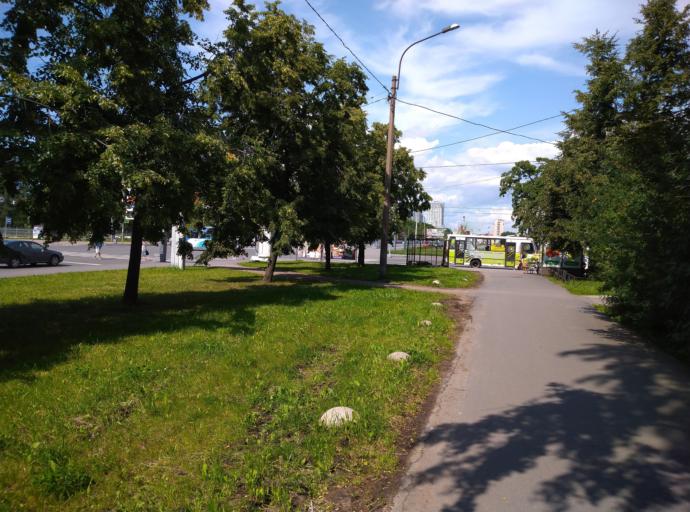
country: RU
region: St.-Petersburg
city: Kupchino
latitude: 59.8640
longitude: 30.3377
